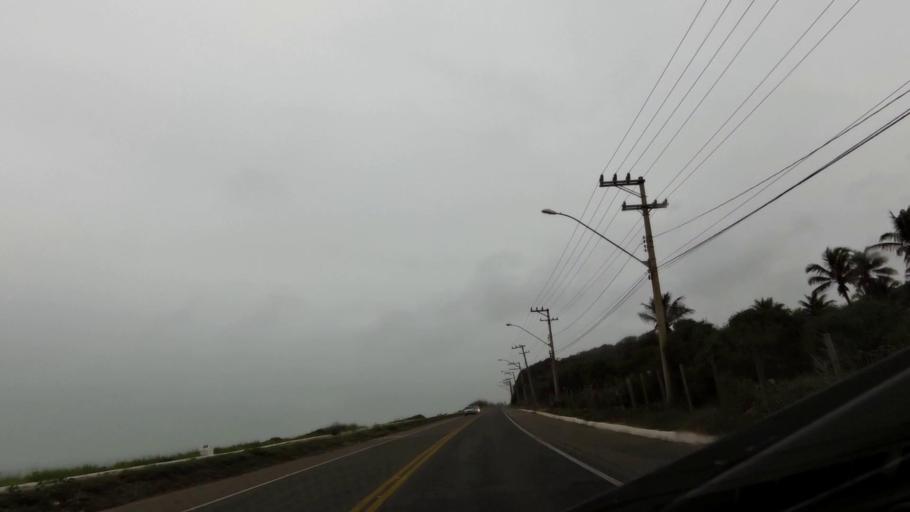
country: BR
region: Espirito Santo
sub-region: Guarapari
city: Guarapari
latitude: -20.7012
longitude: -40.5151
